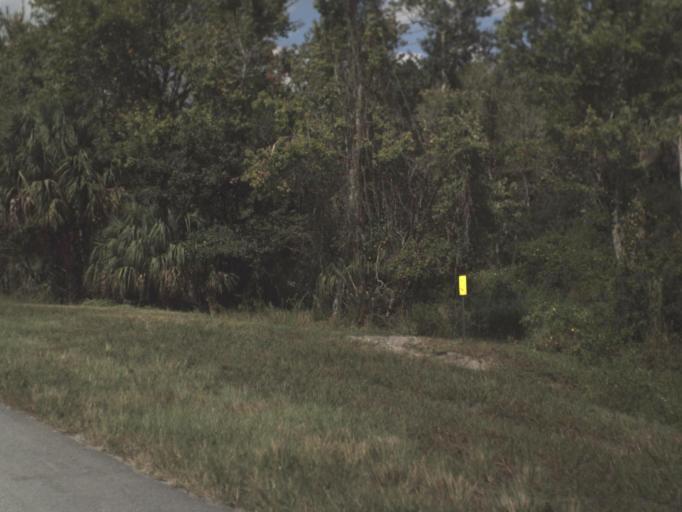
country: US
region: Florida
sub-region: Okeechobee County
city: Cypress Quarters
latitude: 27.5355
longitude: -80.8092
